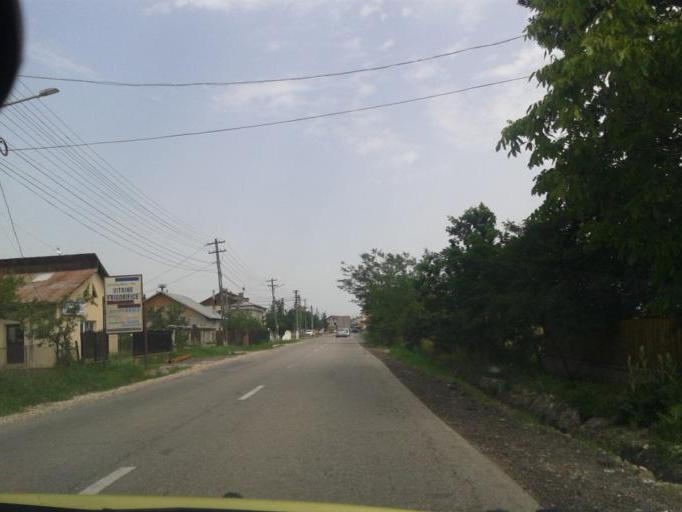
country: RO
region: Dambovita
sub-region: Comuna Petresti
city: Petresti
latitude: 44.6762
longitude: 25.3108
